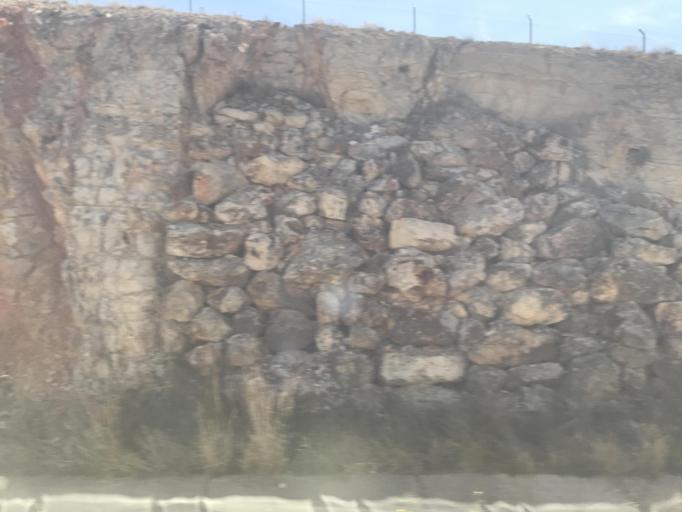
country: ES
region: Castille-La Mancha
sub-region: Provincia de Guadalajara
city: Anguita
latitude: 41.1267
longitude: -2.3408
